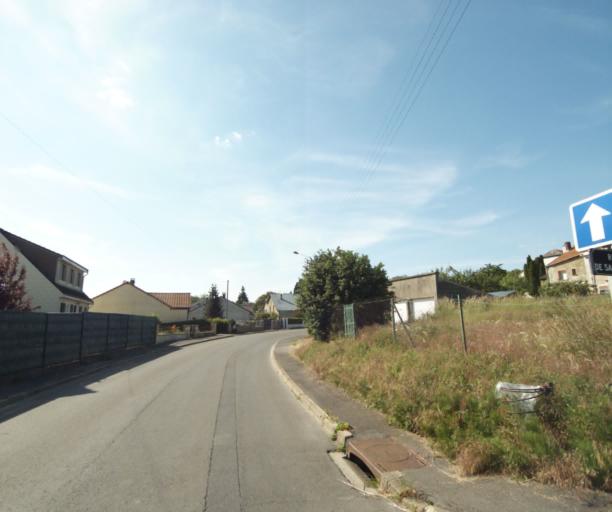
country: FR
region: Champagne-Ardenne
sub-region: Departement des Ardennes
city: Warcq
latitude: 49.7863
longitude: 4.6942
